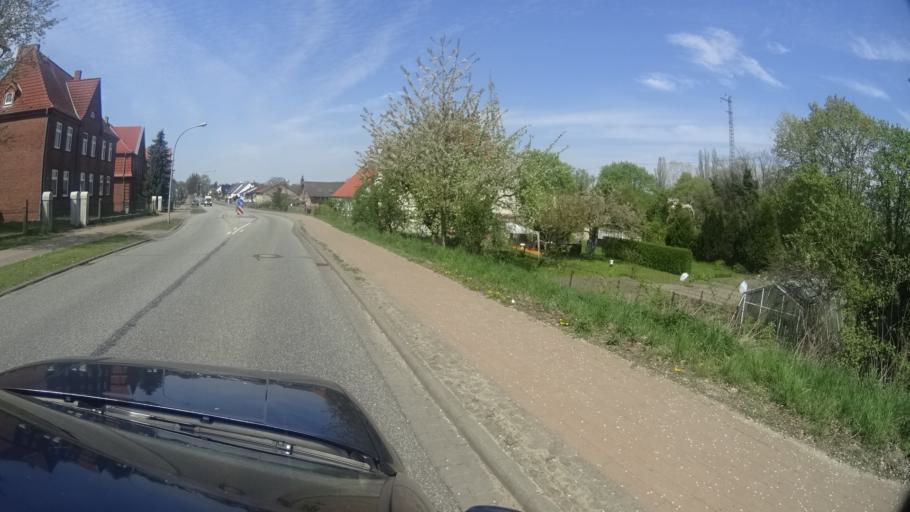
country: DE
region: Brandenburg
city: Wusterhausen
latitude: 52.8549
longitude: 12.4464
